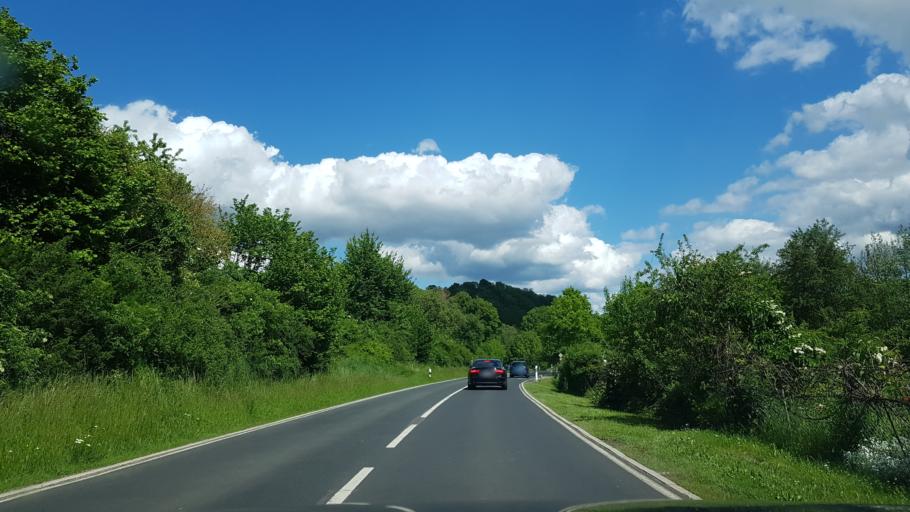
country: DE
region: Hesse
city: Grebenstein
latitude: 51.4412
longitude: 9.4047
